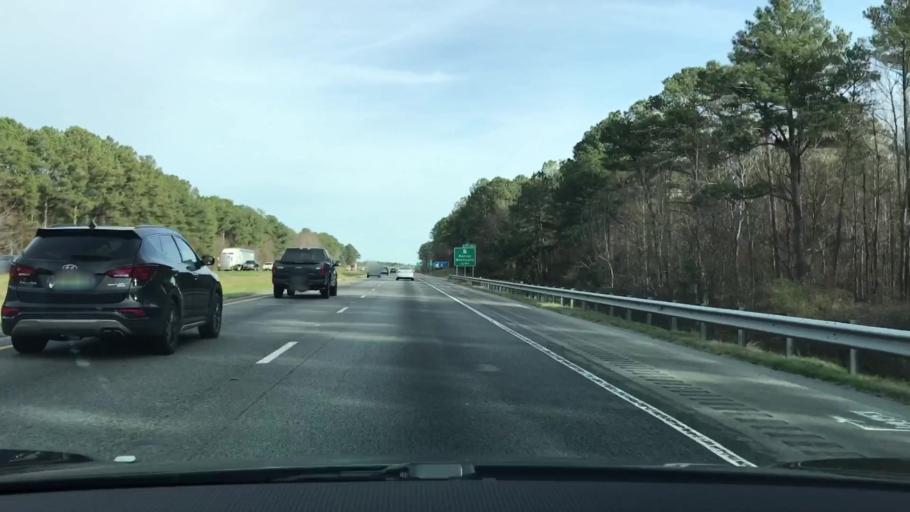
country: US
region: Georgia
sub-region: Walton County
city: Social Circle
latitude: 33.6113
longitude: -83.7654
